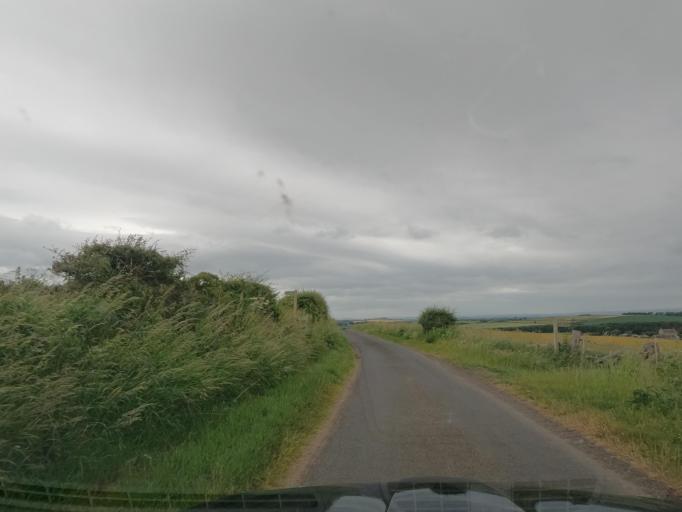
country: GB
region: England
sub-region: Northumberland
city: Ford
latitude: 55.6674
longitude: -2.0892
